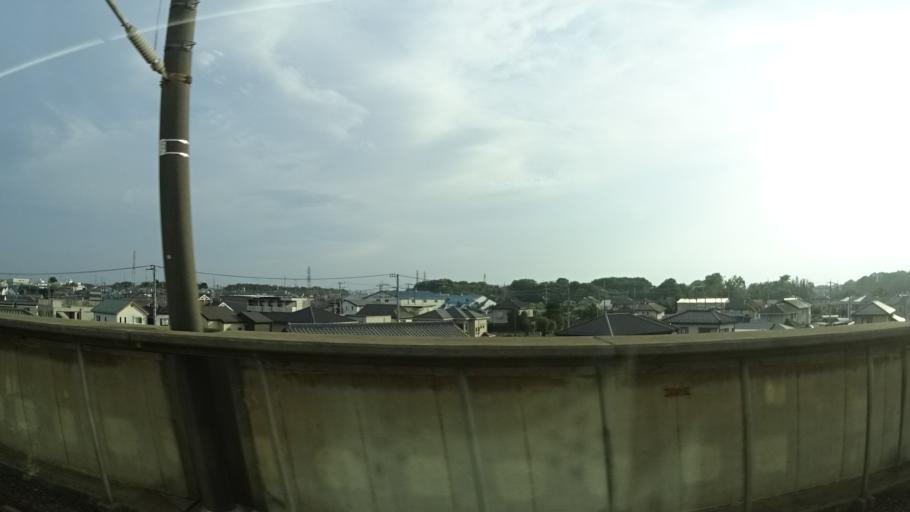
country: JP
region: Saitama
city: Ageoshimo
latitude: 36.0128
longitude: 139.6019
